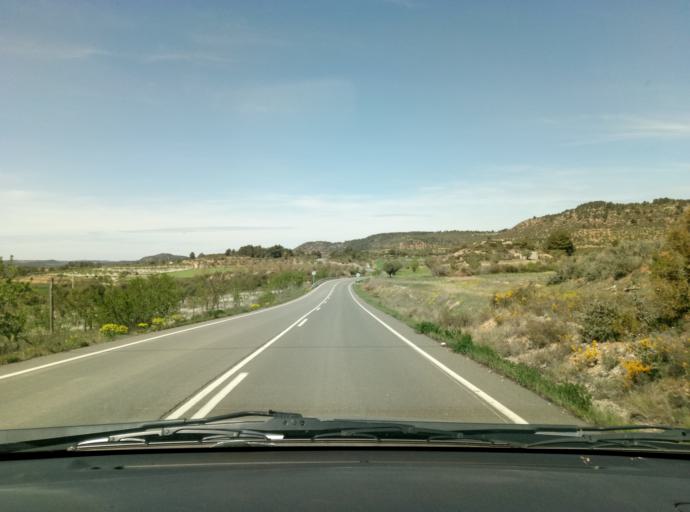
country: ES
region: Catalonia
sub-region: Provincia de Lleida
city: Vinaixa
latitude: 41.4221
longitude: 0.9201
